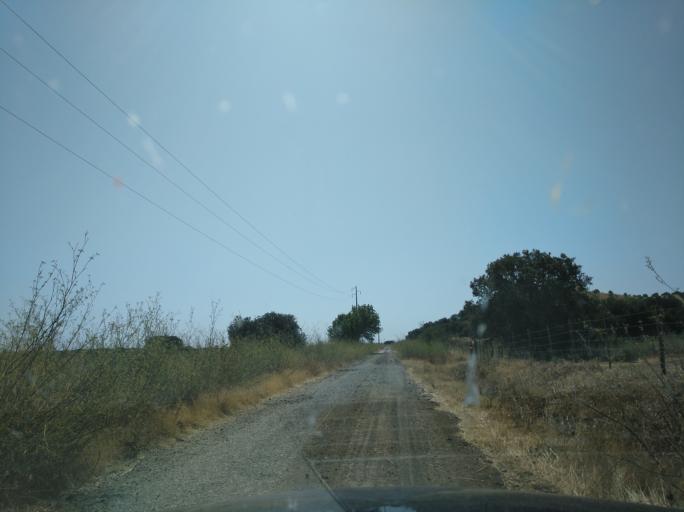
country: PT
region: Portalegre
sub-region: Campo Maior
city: Campo Maior
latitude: 39.0578
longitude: -7.0057
